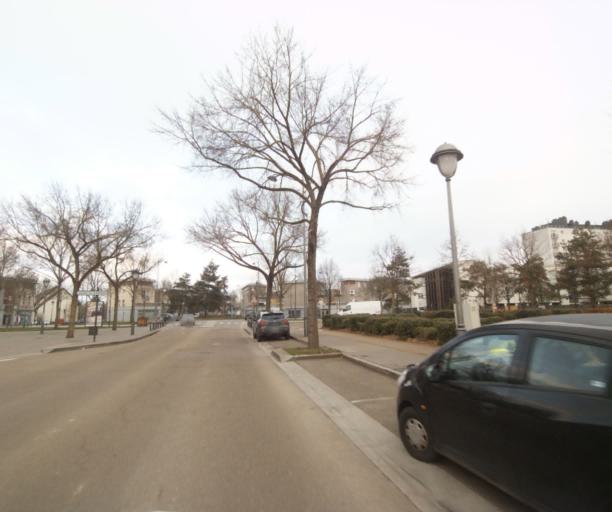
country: FR
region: Champagne-Ardenne
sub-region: Departement de la Haute-Marne
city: Bettancourt-la-Ferree
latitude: 48.6439
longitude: 4.9645
